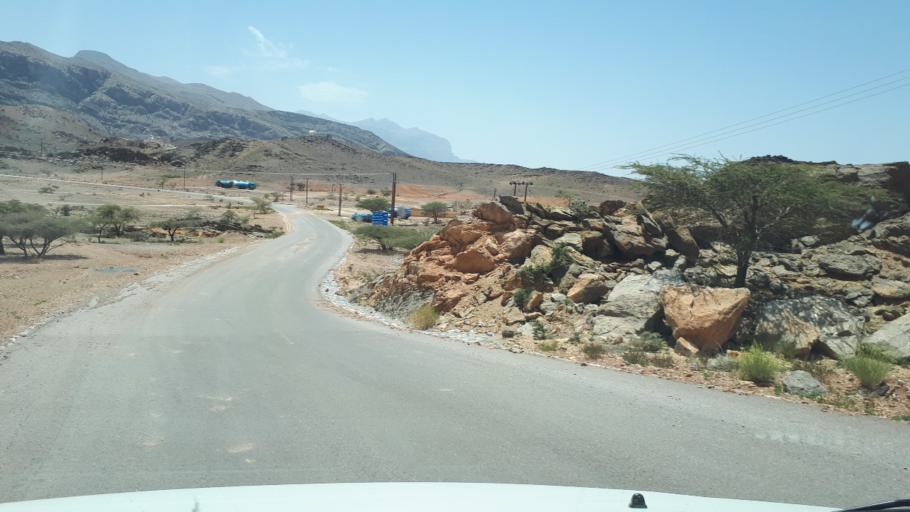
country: OM
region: Muhafazat ad Dakhiliyah
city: Bahla'
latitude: 23.2427
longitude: 57.1518
